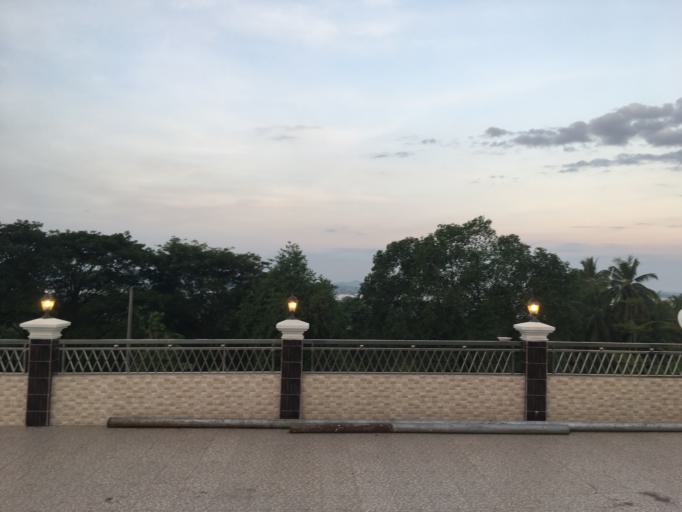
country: MM
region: Mon
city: Mawlamyine
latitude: 16.4922
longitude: 97.6277
